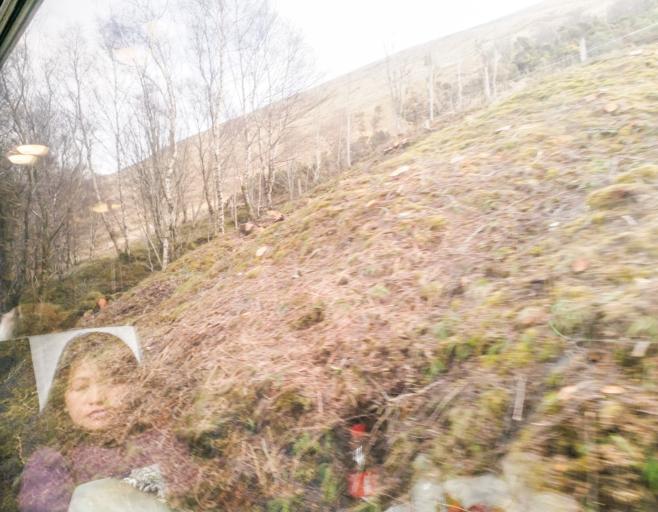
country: GB
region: Scotland
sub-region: Highland
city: Spean Bridge
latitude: 56.8049
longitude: -4.7190
